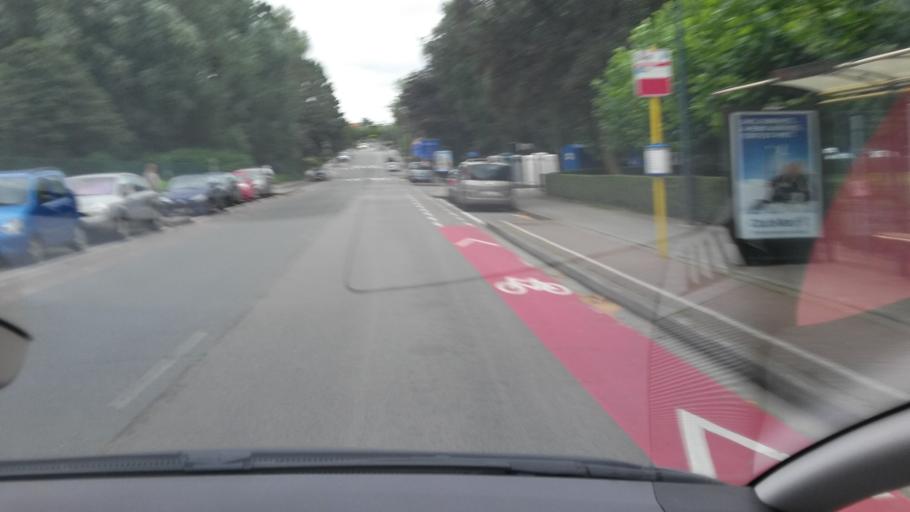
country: BE
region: Flanders
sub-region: Provincie Vlaams-Brabant
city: Hoeilaart
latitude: 50.8130
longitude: 4.4173
